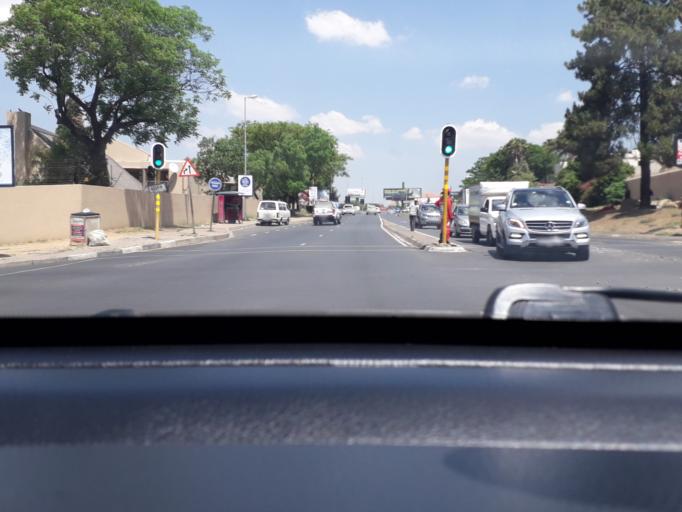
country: ZA
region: Gauteng
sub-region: City of Johannesburg Metropolitan Municipality
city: Modderfontein
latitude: -26.0721
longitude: 28.0643
